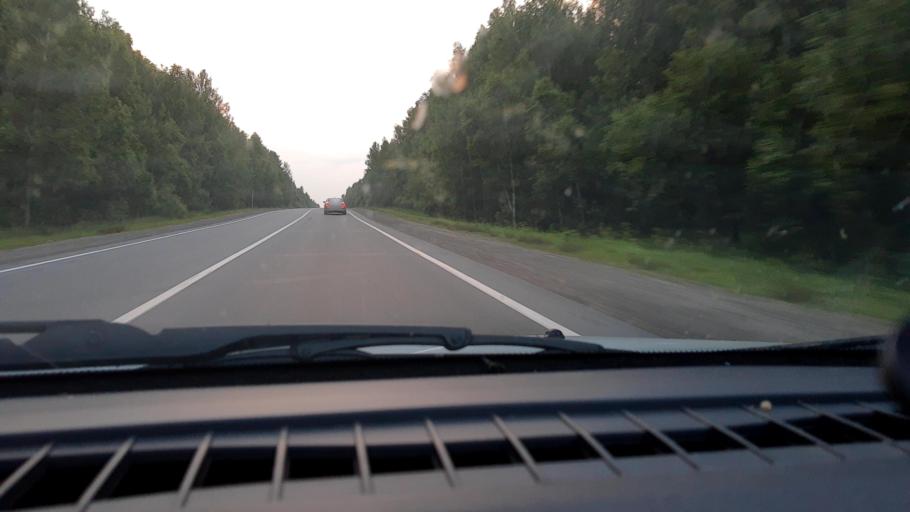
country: RU
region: Nizjnij Novgorod
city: Surovatikha
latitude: 55.5759
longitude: 43.9677
